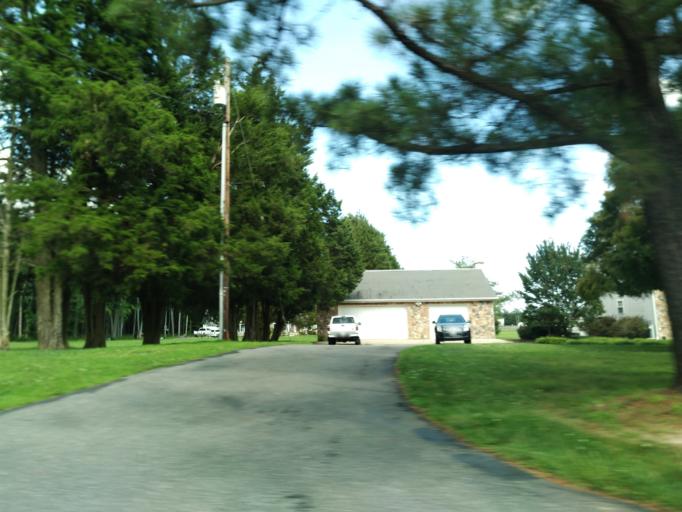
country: US
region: Maryland
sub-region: Anne Arundel County
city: Deale
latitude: 38.7952
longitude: -76.5738
